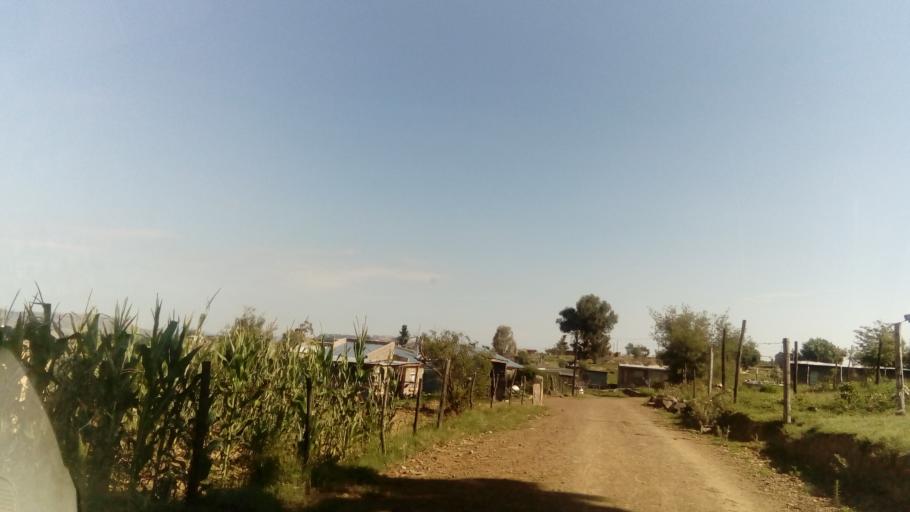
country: LS
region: Berea
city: Teyateyaneng
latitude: -29.1398
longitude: 27.7484
